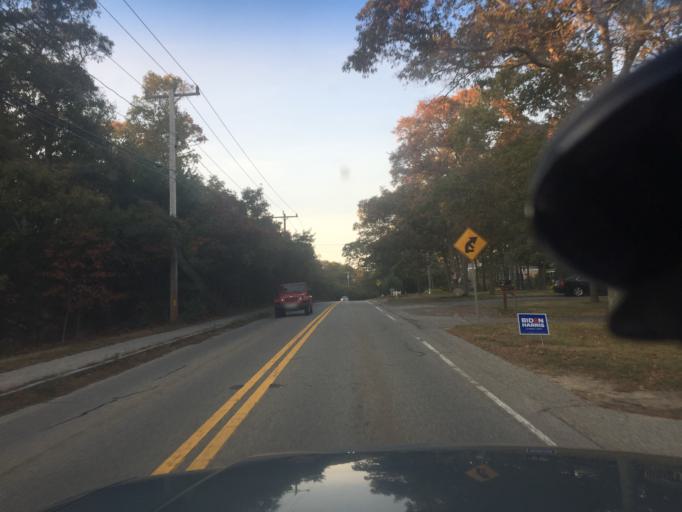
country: US
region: Massachusetts
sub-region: Barnstable County
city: North Falmouth
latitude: 41.6526
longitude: -70.6123
